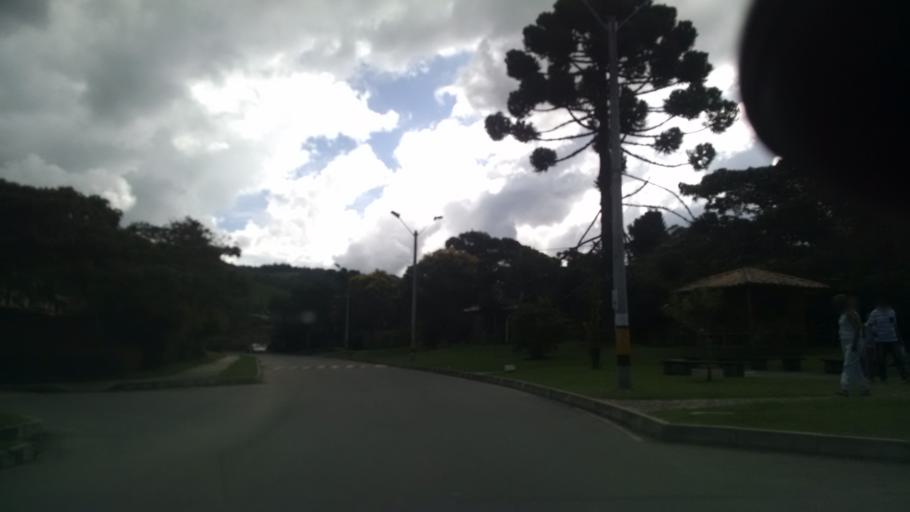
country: CO
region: Antioquia
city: El Retiro
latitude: 6.0580
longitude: -75.5062
